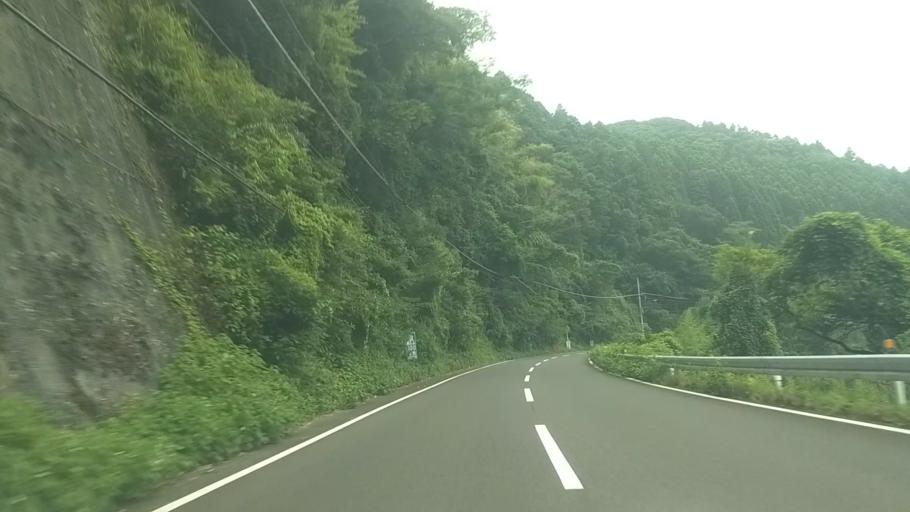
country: JP
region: Chiba
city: Katsuura
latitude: 35.2455
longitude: 140.2410
